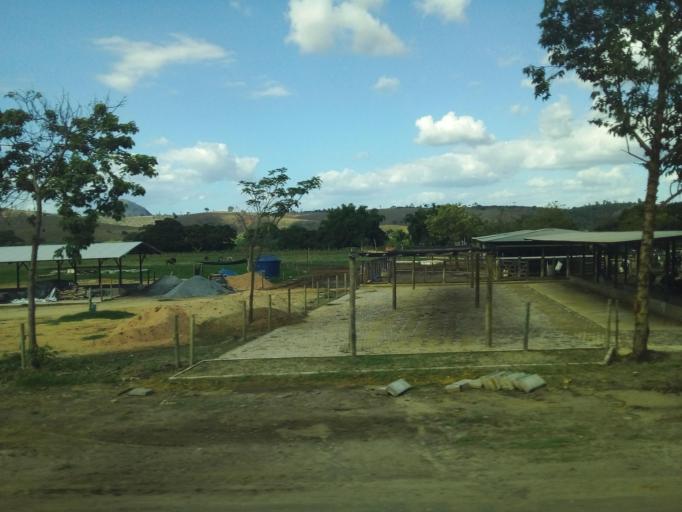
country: BR
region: Minas Gerais
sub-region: Conselheiro Pena
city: Conselheiro Pena
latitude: -18.9937
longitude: -41.5965
